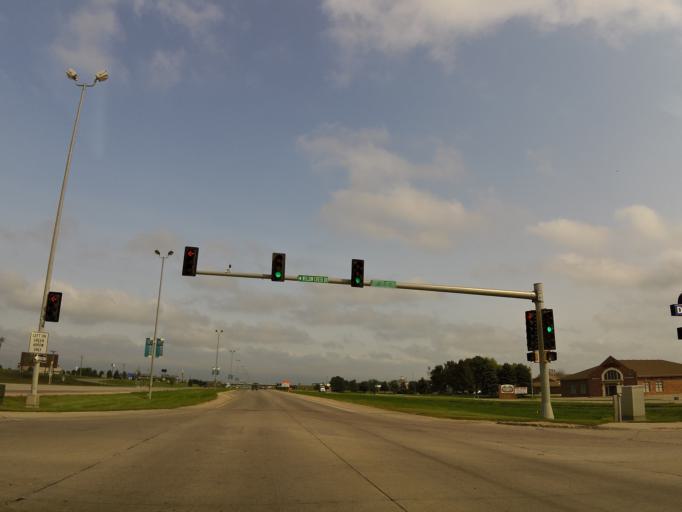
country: US
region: South Dakota
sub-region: Codington County
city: Watertown
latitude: 44.8900
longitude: -97.0682
